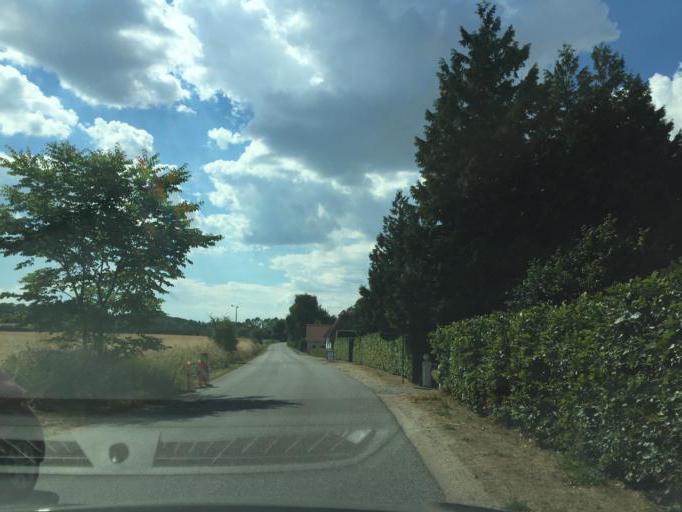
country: DK
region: South Denmark
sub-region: Assens Kommune
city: Harby
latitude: 55.2096
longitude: 10.0852
